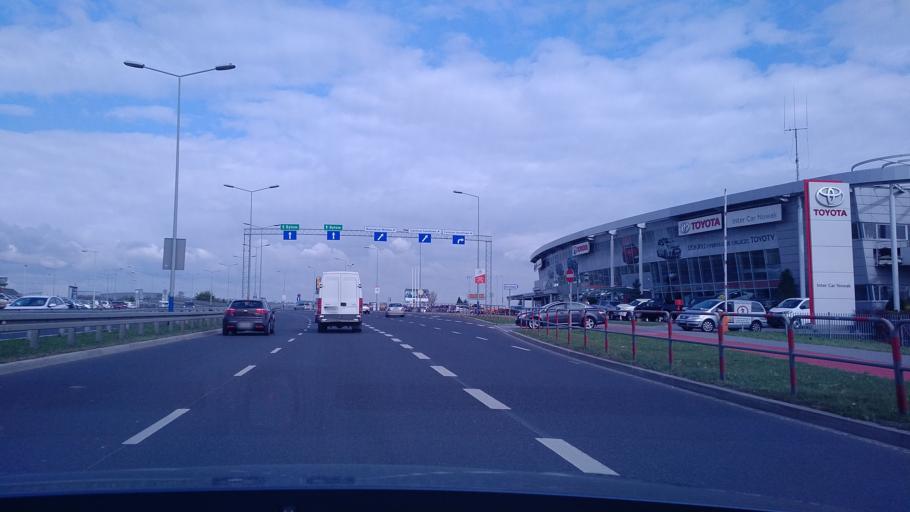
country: PL
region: Lesser Poland Voivodeship
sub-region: Powiat krakowski
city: Zielonki
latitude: 50.0908
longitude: 19.8932
